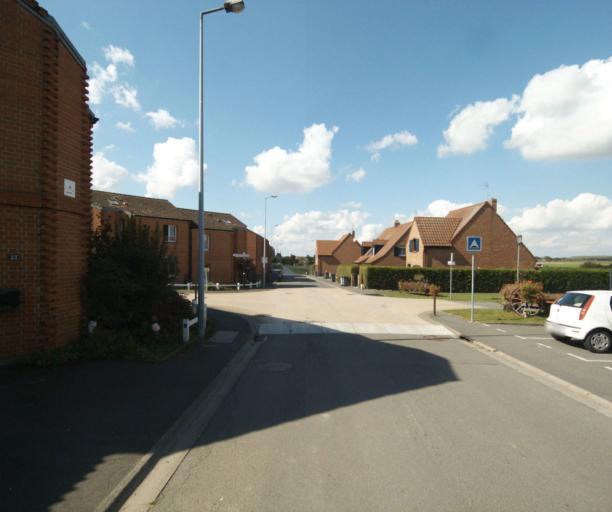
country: FR
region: Nord-Pas-de-Calais
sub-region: Departement du Nord
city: Illies
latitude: 50.5619
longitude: 2.8284
